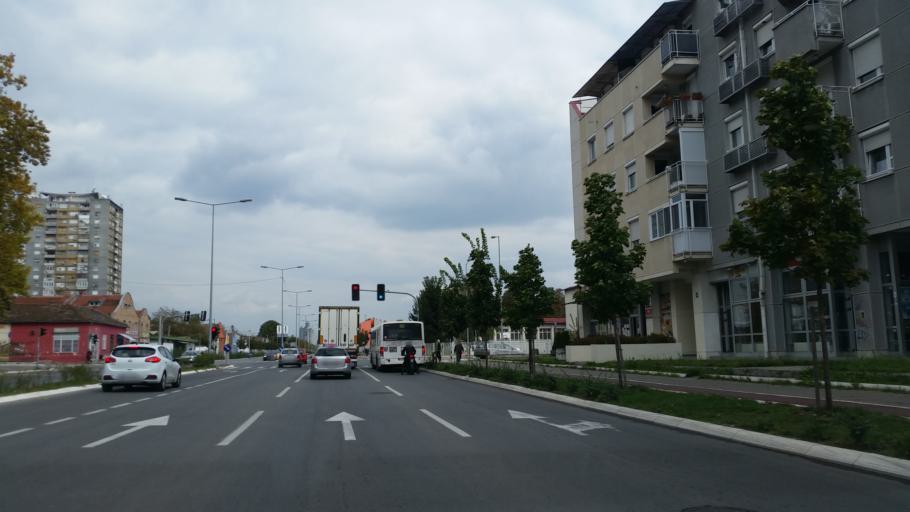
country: RS
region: Central Serbia
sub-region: Belgrade
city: Zemun
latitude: 44.8074
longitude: 20.3755
